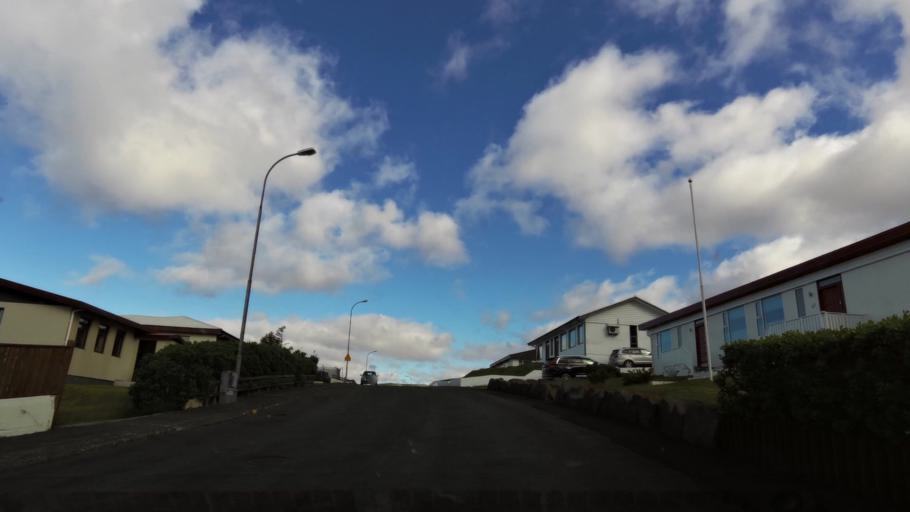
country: IS
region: West
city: Olafsvik
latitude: 64.8910
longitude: -23.7083
